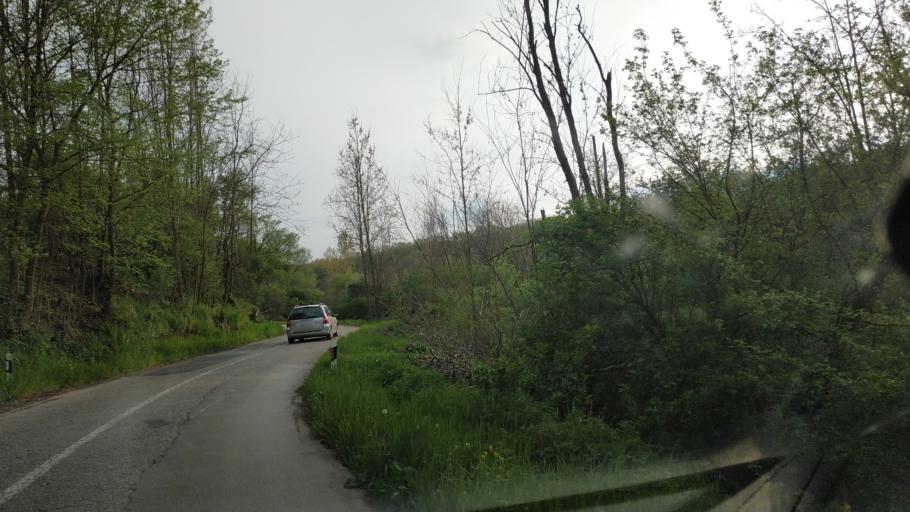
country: RS
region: Central Serbia
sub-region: Nisavski Okrug
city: Aleksinac
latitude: 43.4663
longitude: 21.8054
